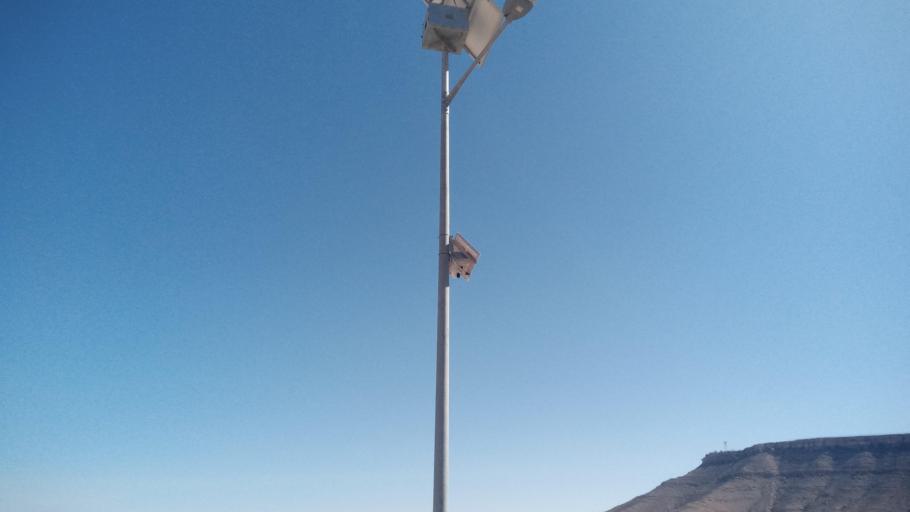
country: TN
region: Madanin
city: Bani Khaddash
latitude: 33.2715
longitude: 10.2759
